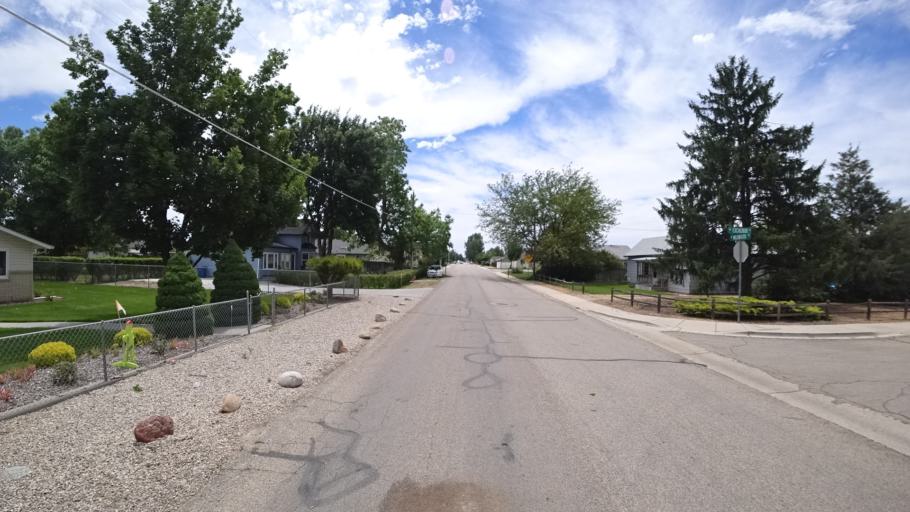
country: US
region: Idaho
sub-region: Ada County
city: Meridian
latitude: 43.6305
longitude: -116.3219
